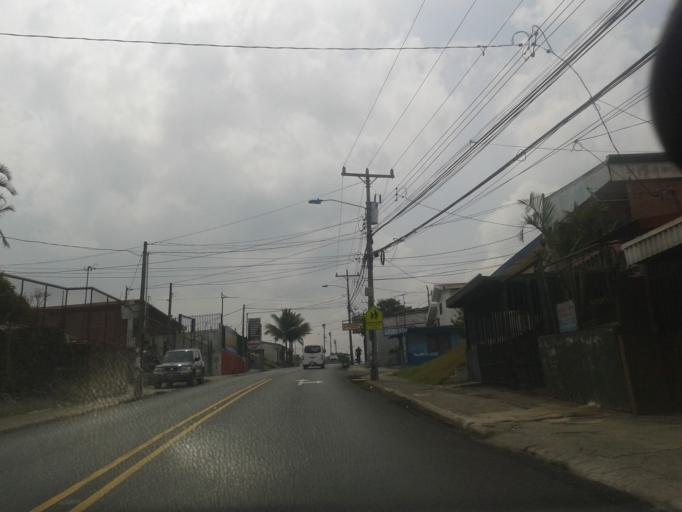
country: CR
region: Heredia
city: Heredia
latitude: 9.9936
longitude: -84.1116
